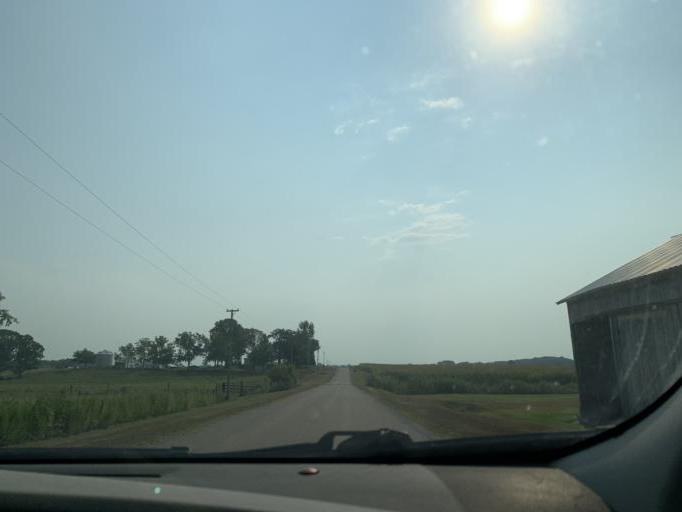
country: US
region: Illinois
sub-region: Whiteside County
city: Morrison
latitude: 41.8698
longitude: -89.9065
